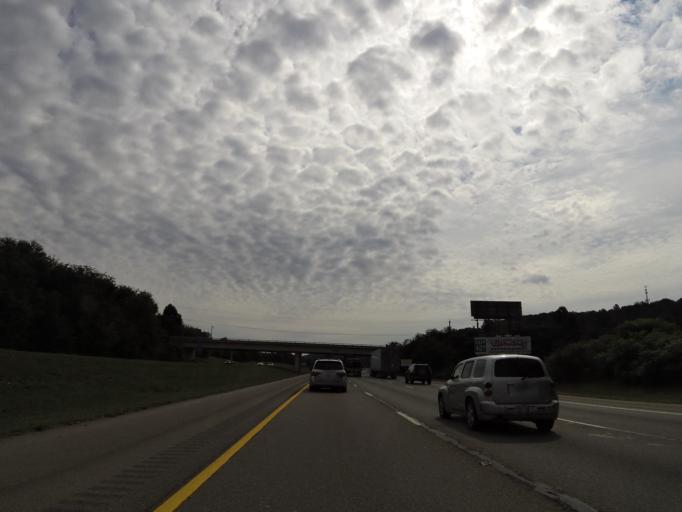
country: US
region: Tennessee
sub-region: Knox County
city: Mascot
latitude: 36.0051
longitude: -83.7522
